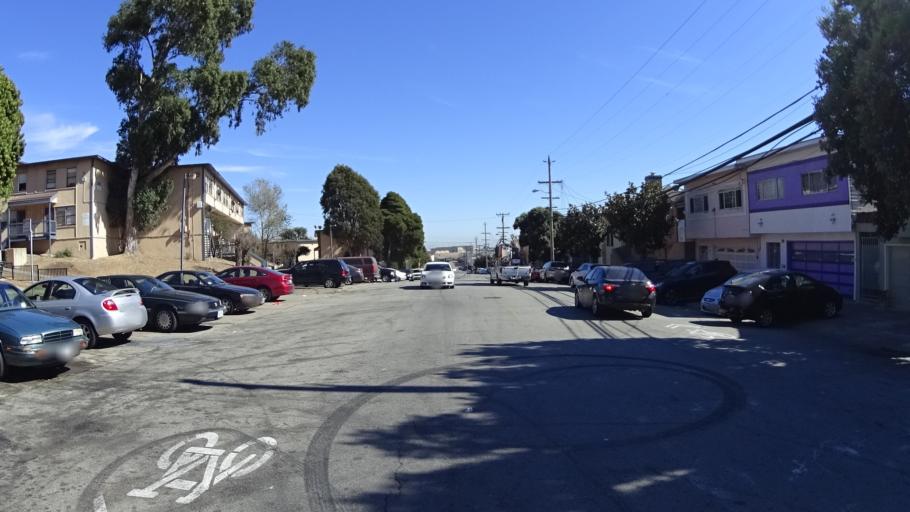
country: US
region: California
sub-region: San Mateo County
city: Brisbane
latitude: 37.7293
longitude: -122.3826
